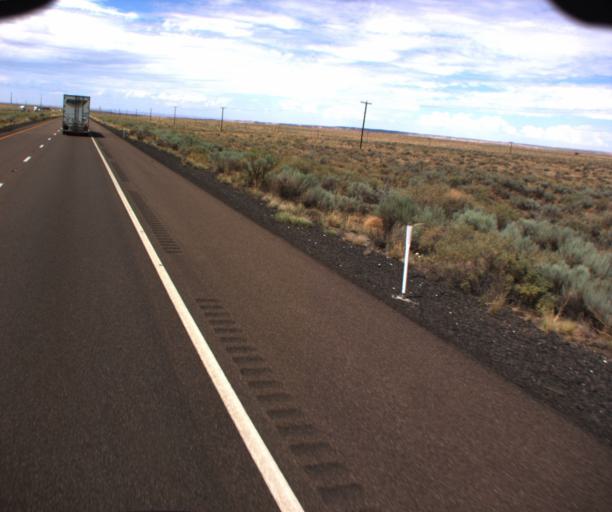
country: US
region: Arizona
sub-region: Navajo County
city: Holbrook
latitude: 35.0447
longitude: -109.8090
